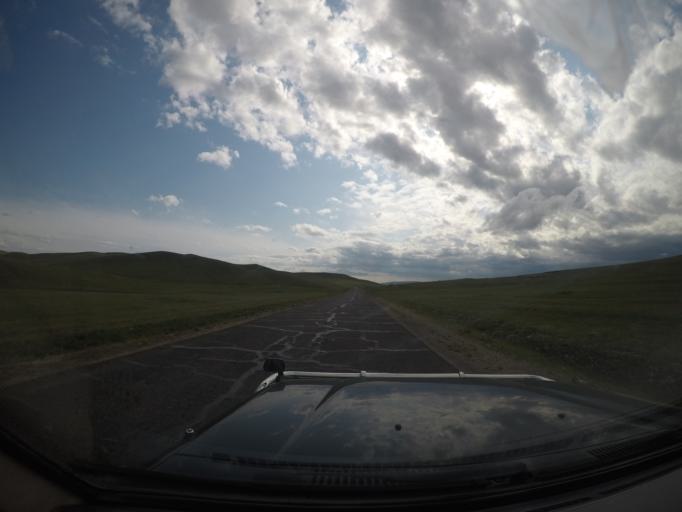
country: MN
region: Hentiy
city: Modot
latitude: 47.7998
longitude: 108.6978
